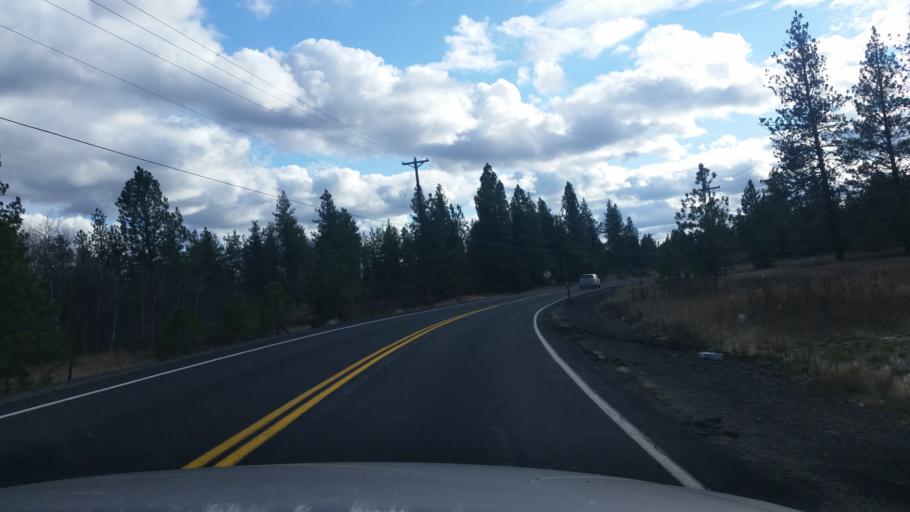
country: US
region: Washington
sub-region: Spokane County
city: Cheney
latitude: 47.4803
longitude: -117.5796
